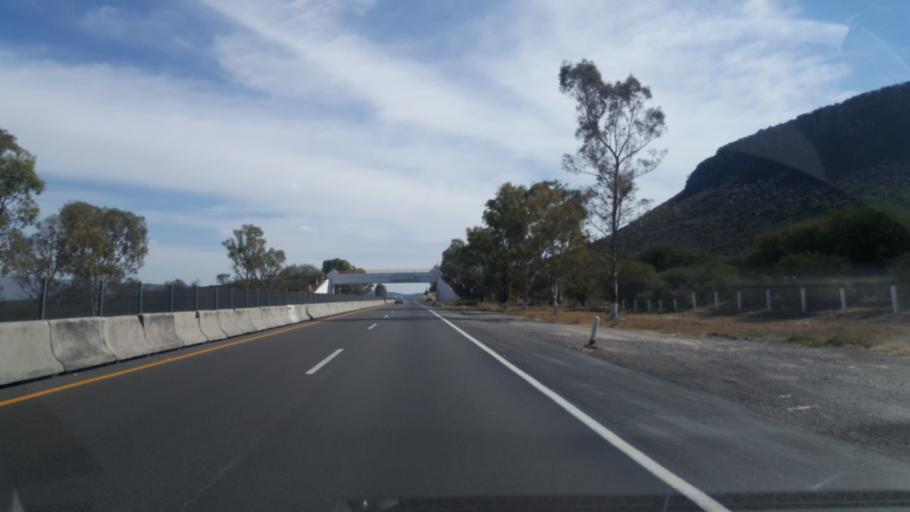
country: MX
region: Jalisco
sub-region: Lagos de Moreno
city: Cristeros [Fraccionamiento]
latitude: 21.2938
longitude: -102.0110
